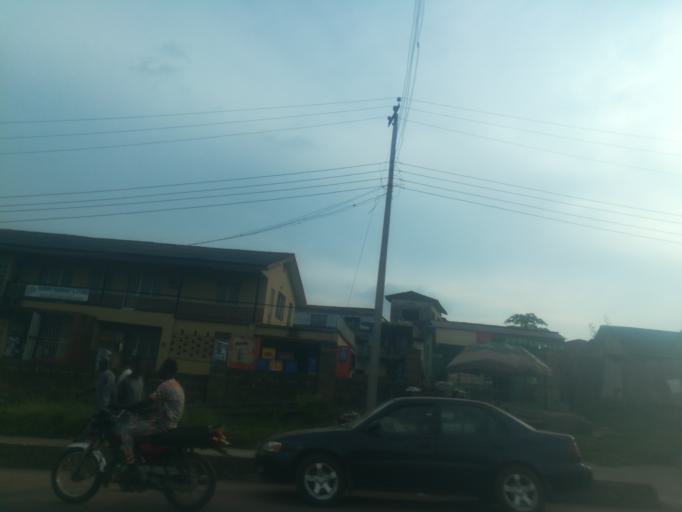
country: NG
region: Ogun
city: Abeokuta
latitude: 7.1628
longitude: 3.3151
